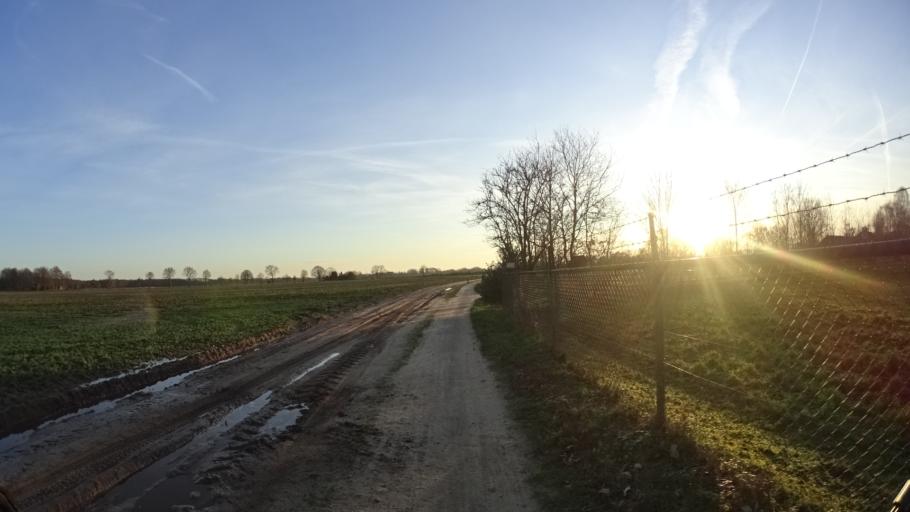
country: NL
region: Gelderland
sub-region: Gemeente Ede
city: Lunteren
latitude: 52.0735
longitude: 5.6444
